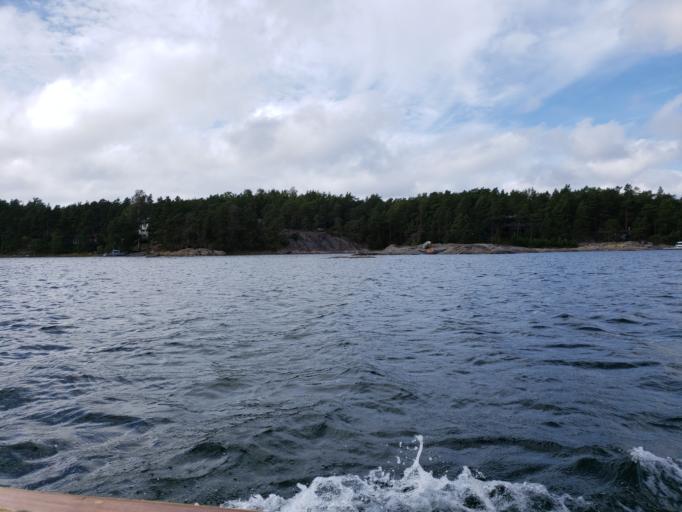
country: FI
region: Varsinais-Suomi
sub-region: Aboland-Turunmaa
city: Dragsfjaerd
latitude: 59.9077
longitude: 22.3747
